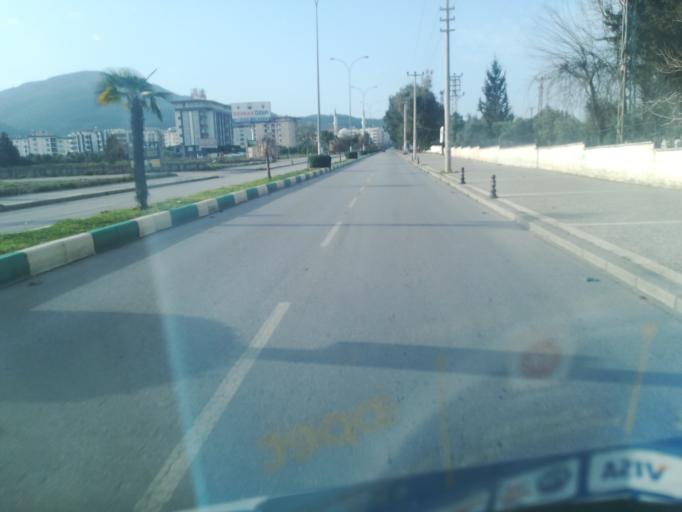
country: TR
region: Osmaniye
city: Osmaniye
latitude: 37.0484
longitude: 36.2273
